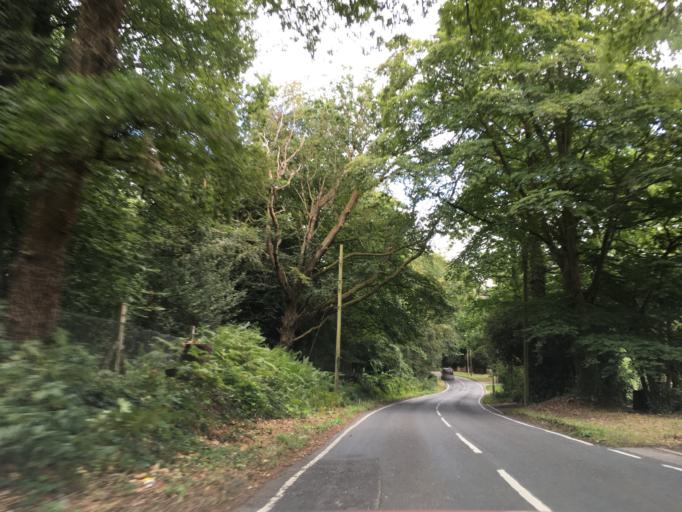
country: GB
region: England
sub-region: Hampshire
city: Chandlers Ford
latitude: 50.9994
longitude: -1.3614
